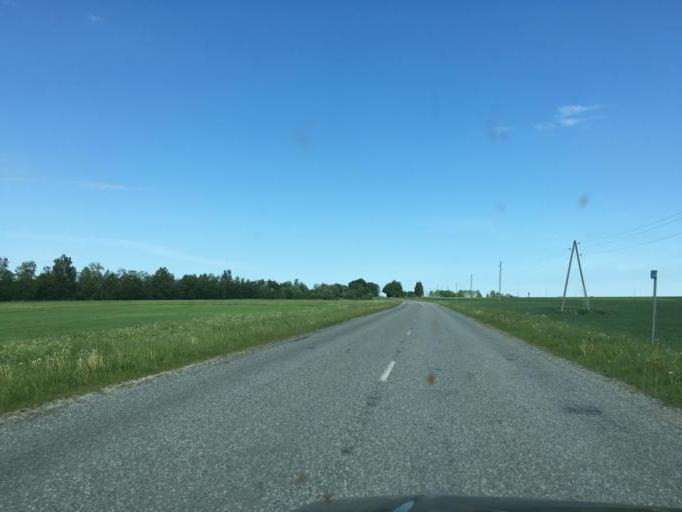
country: LV
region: Talsu Rajons
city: Valdemarpils
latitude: 57.3690
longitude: 22.4853
